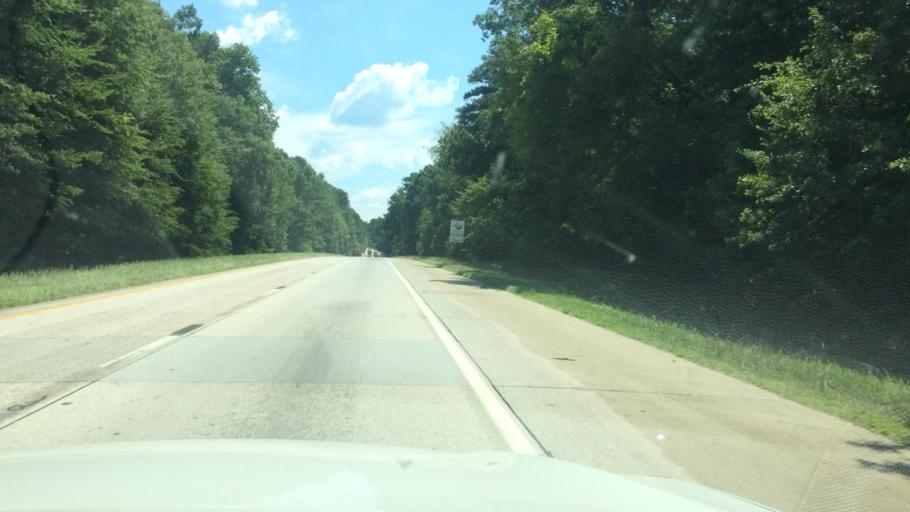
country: US
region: South Carolina
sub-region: Aiken County
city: Belvedere
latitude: 33.5427
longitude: -81.9810
